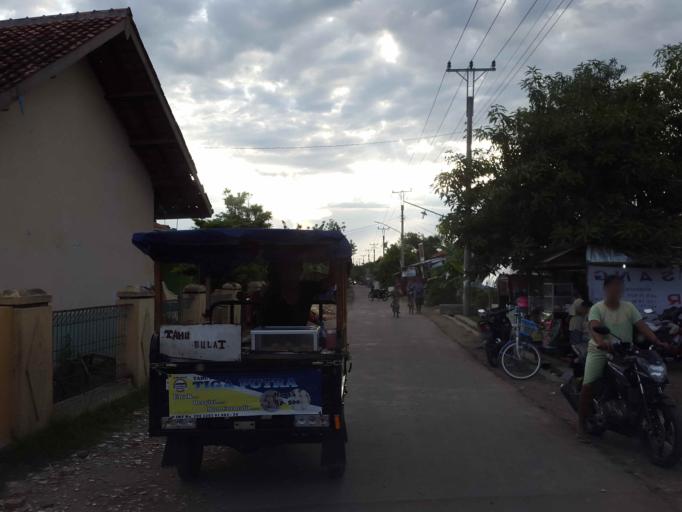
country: ID
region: Central Java
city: Ketanggungan
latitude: -6.9062
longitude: 108.8737
